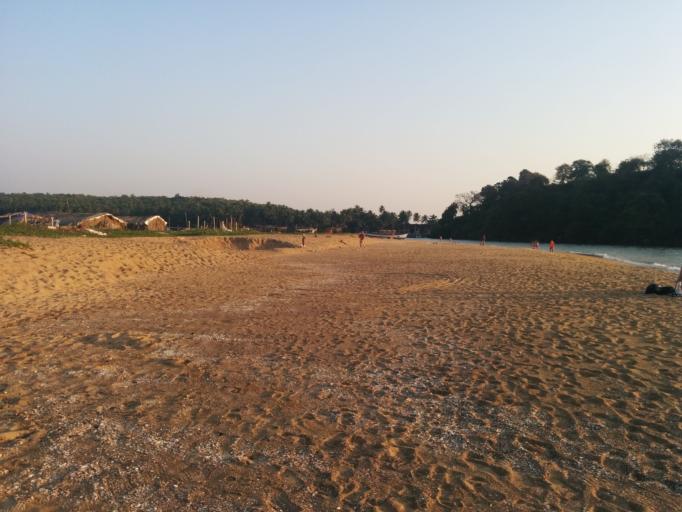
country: IN
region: Karnataka
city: Canacona
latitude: 14.9863
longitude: 74.0382
